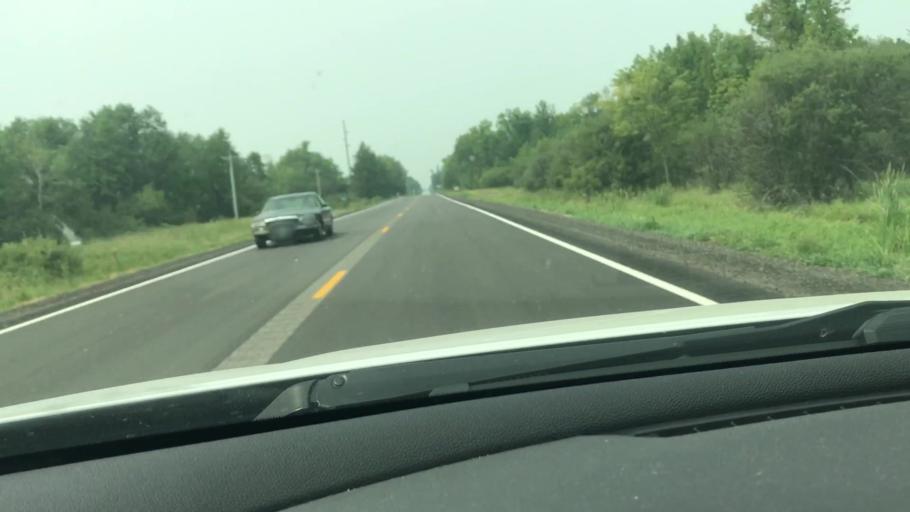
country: US
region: Minnesota
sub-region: Itasca County
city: Cohasset
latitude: 47.3642
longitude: -93.8719
